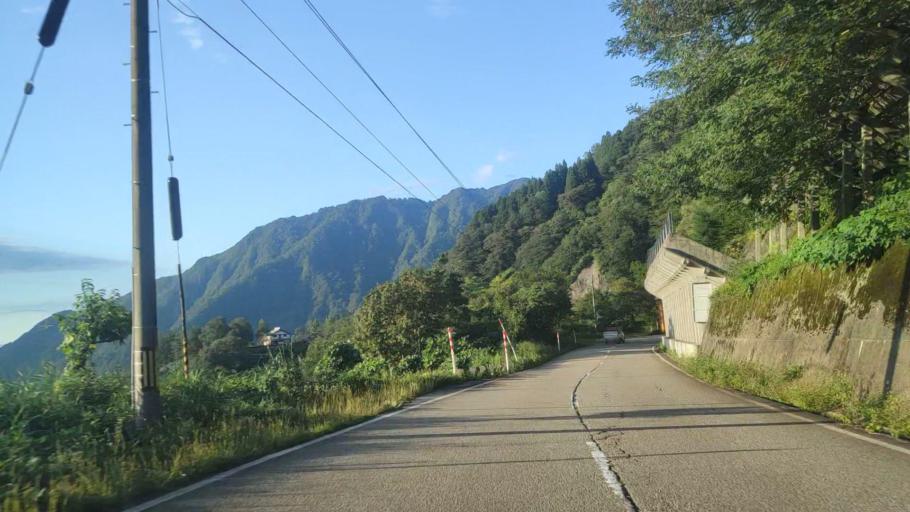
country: JP
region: Toyama
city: Yatsuomachi-higashikumisaka
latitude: 36.5205
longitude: 137.0281
